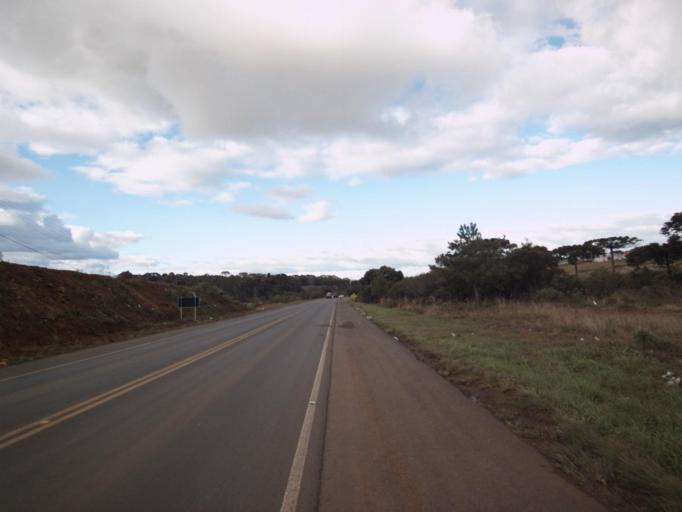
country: BR
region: Santa Catarina
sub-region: Campos Novos
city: Campos Novos
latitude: -27.3886
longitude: -51.2088
